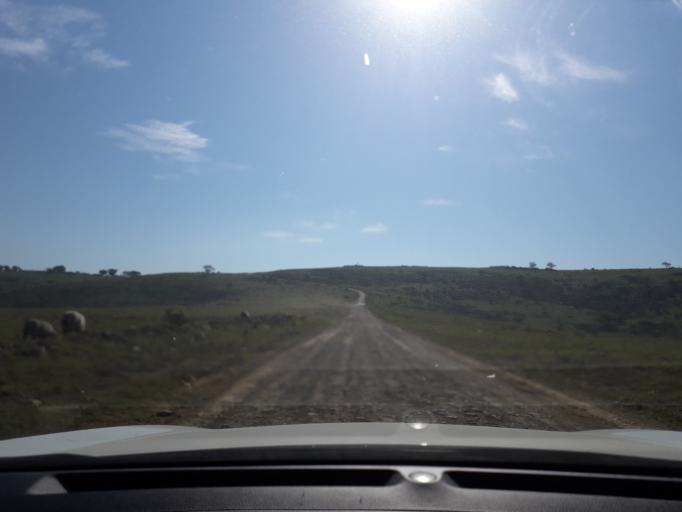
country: ZA
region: Eastern Cape
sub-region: Buffalo City Metropolitan Municipality
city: Bhisho
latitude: -32.9816
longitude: 27.3232
